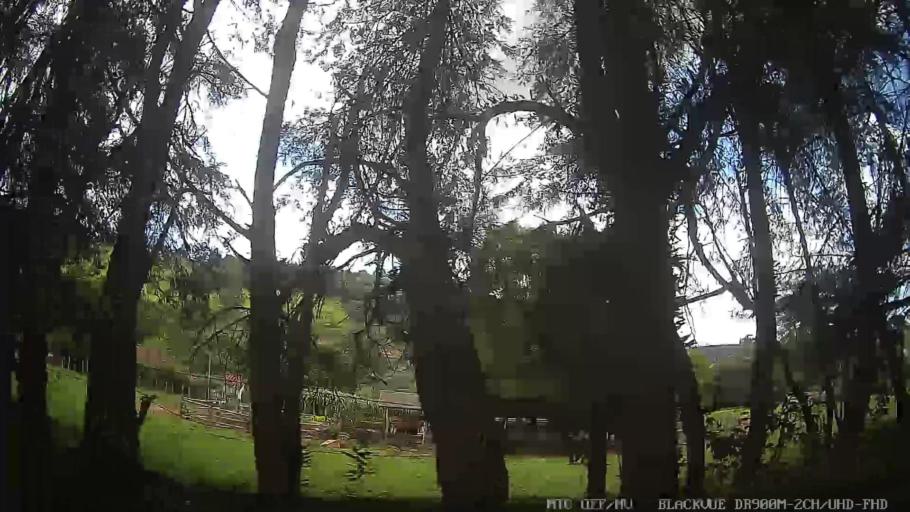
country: BR
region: Sao Paulo
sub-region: Braganca Paulista
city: Braganca Paulista
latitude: -23.0180
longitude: -46.4945
